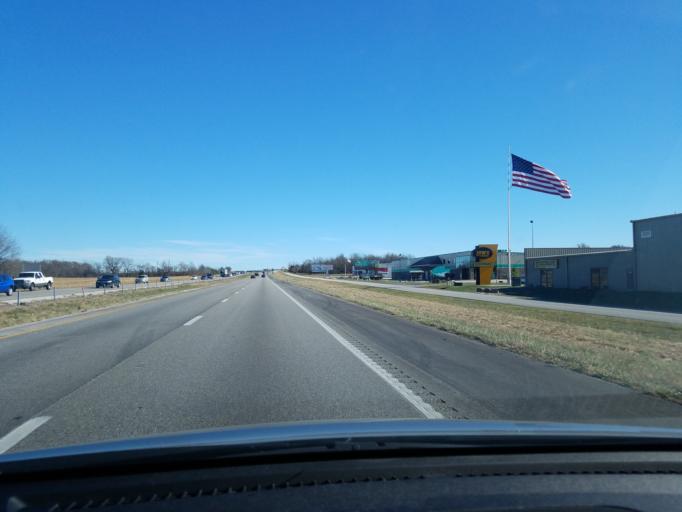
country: US
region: Missouri
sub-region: Greene County
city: Strafford
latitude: 37.2501
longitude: -93.1976
